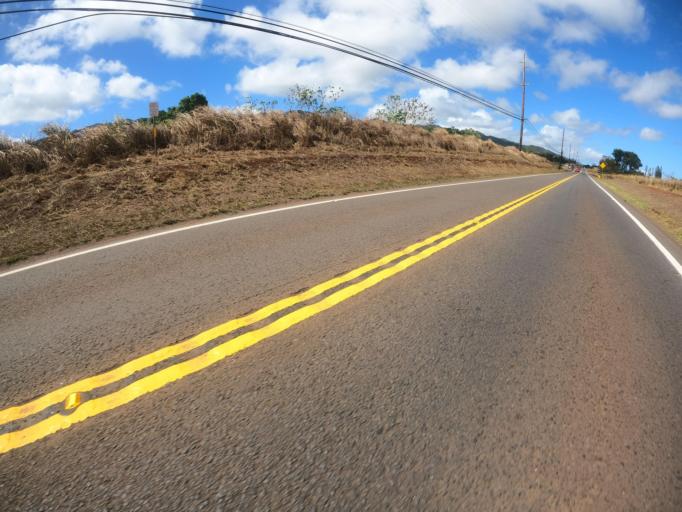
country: US
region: Hawaii
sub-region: Honolulu County
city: Village Park
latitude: 21.4284
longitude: -158.0552
